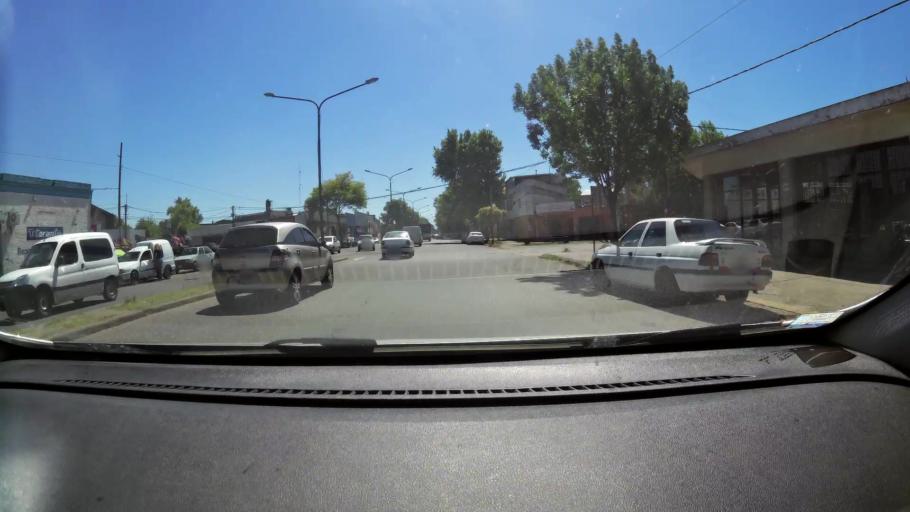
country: AR
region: Santa Fe
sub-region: Departamento de Rosario
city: Rosario
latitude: -32.9653
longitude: -60.7060
